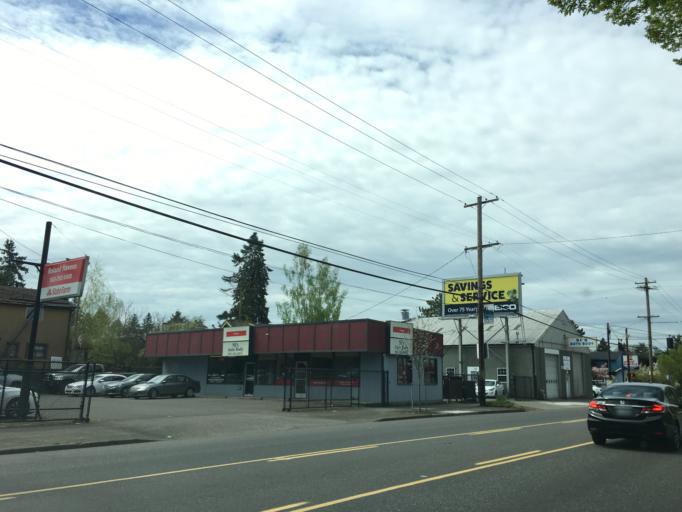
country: US
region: Oregon
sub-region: Multnomah County
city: Lents
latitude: 45.5265
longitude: -122.5935
